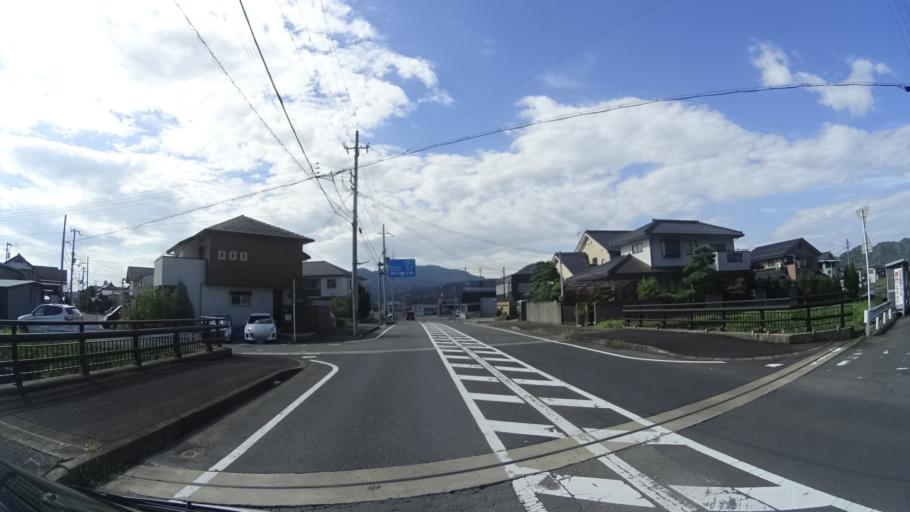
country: JP
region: Kyoto
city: Fukuchiyama
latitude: 35.2999
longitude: 135.1817
